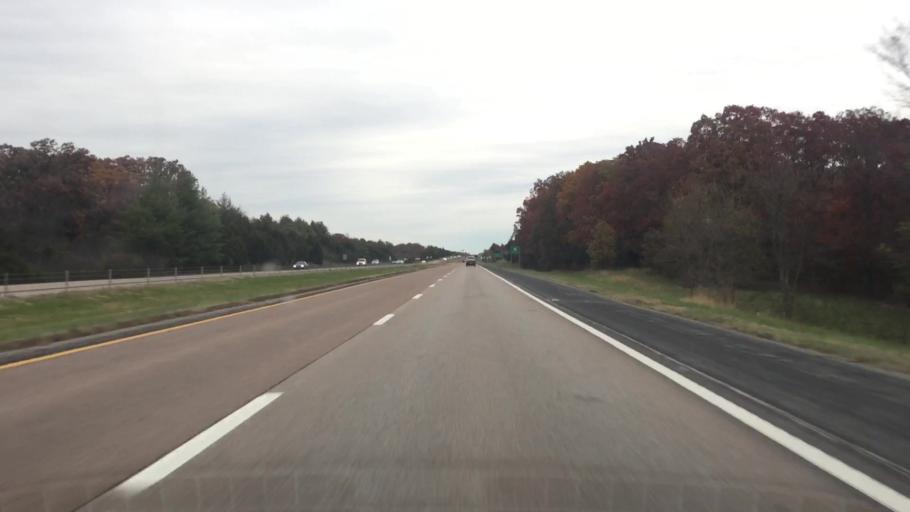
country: US
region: Missouri
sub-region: Boone County
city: Ashland
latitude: 38.7264
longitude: -92.2540
